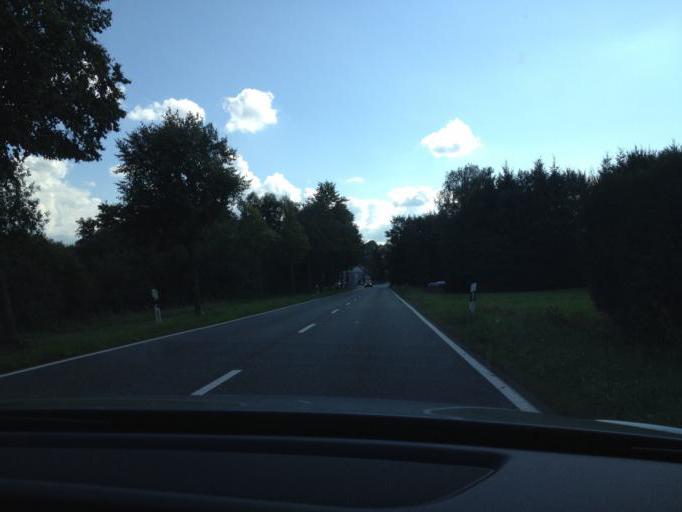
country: DE
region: Saarland
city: Mainzweiler
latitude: 49.4375
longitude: 7.1259
